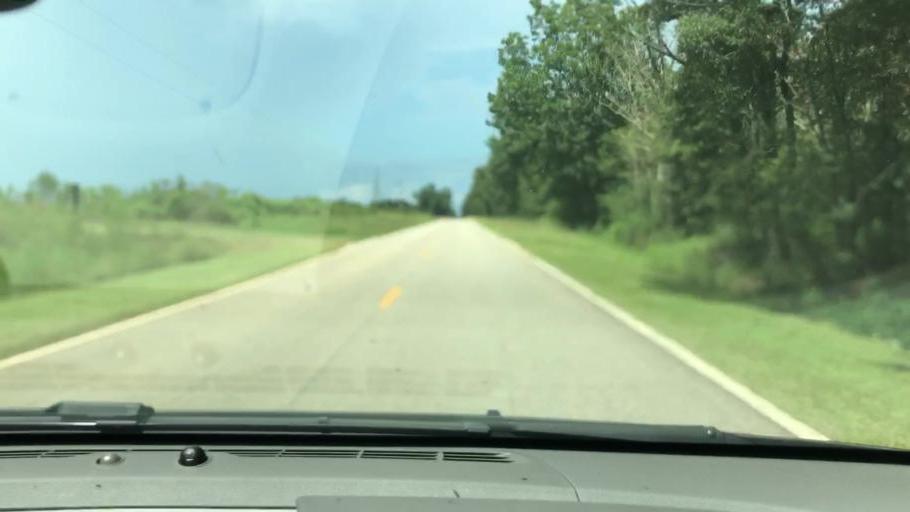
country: US
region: Georgia
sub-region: Seminole County
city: Donalsonville
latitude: 31.1293
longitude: -84.9954
